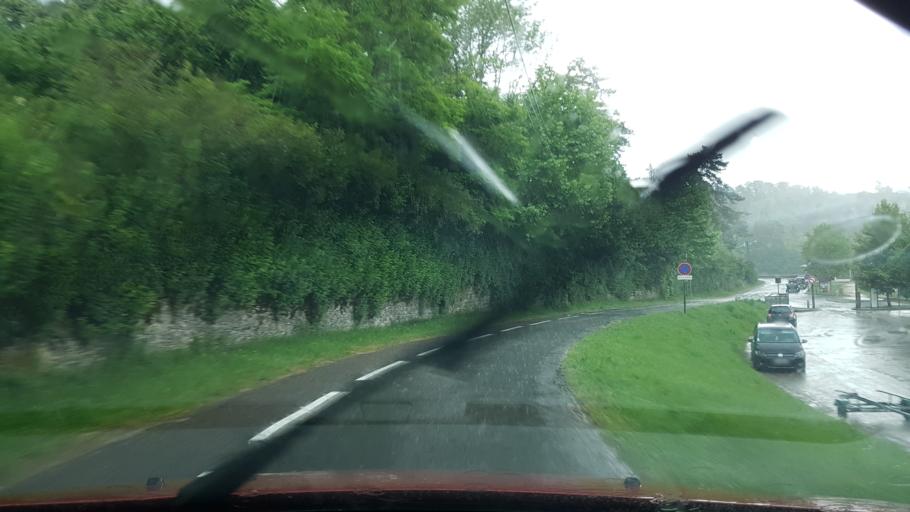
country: FR
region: Franche-Comte
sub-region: Departement du Jura
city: Clairvaux-les-Lacs
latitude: 46.5802
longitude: 5.6994
